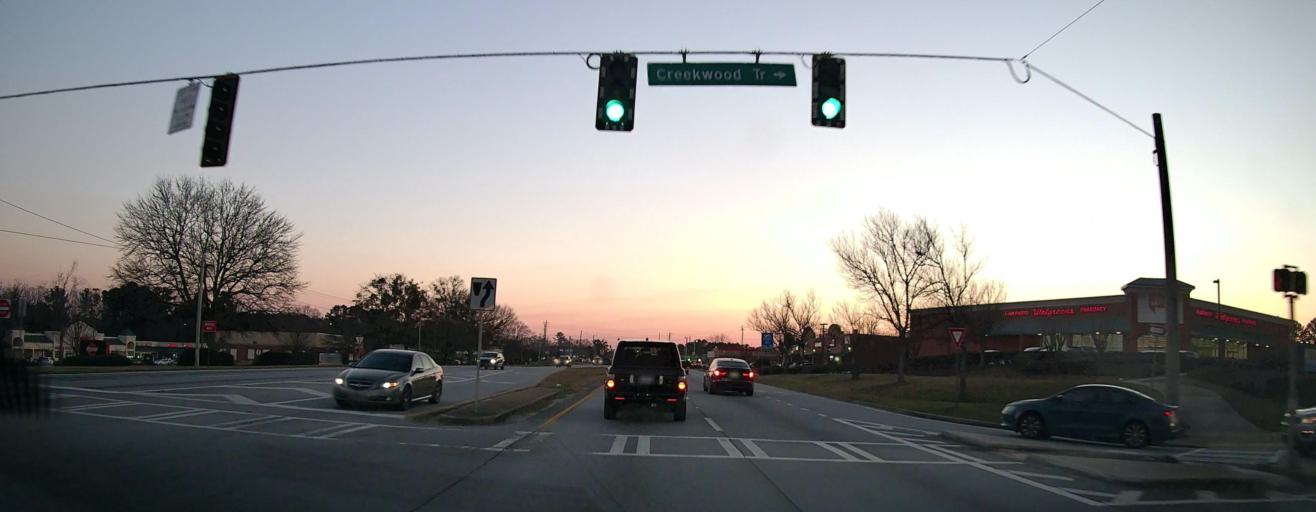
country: US
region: Georgia
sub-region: Fayette County
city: Fayetteville
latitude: 33.4664
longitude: -84.4482
